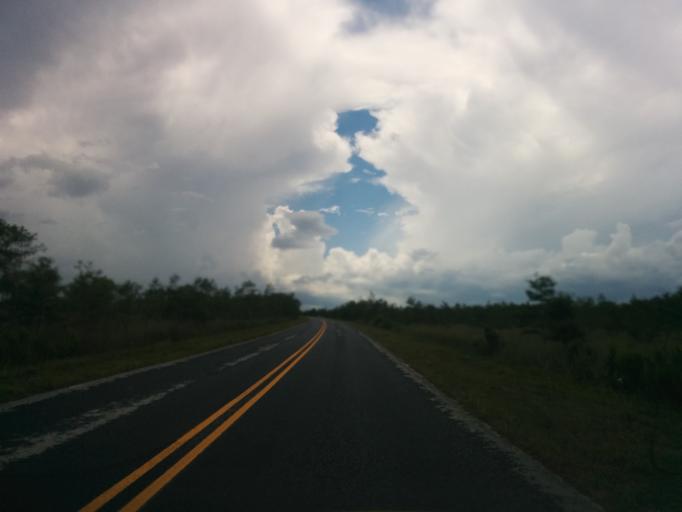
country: US
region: Florida
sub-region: Miami-Dade County
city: Florida City
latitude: 25.4337
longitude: -80.7500
